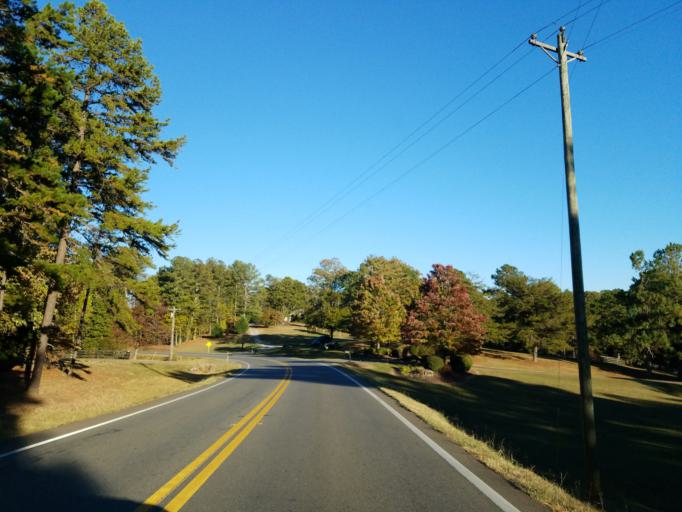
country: US
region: Georgia
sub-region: Dawson County
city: Dawsonville
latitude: 34.4262
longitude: -84.2299
